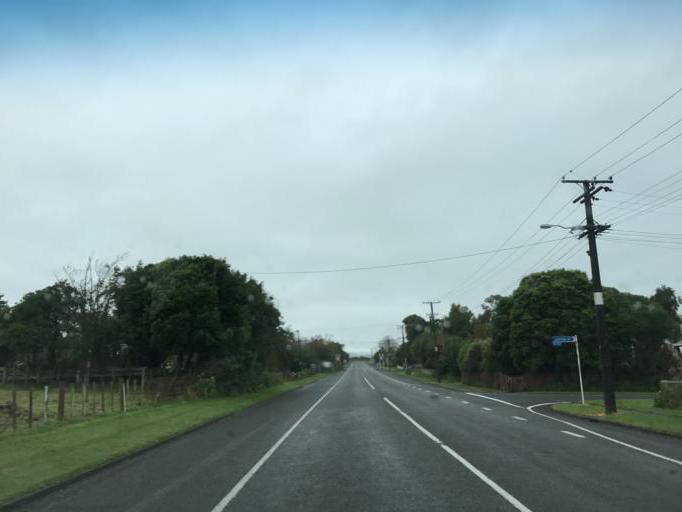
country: NZ
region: Taranaki
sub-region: South Taranaki District
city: Patea
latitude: -39.7637
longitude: 174.6370
